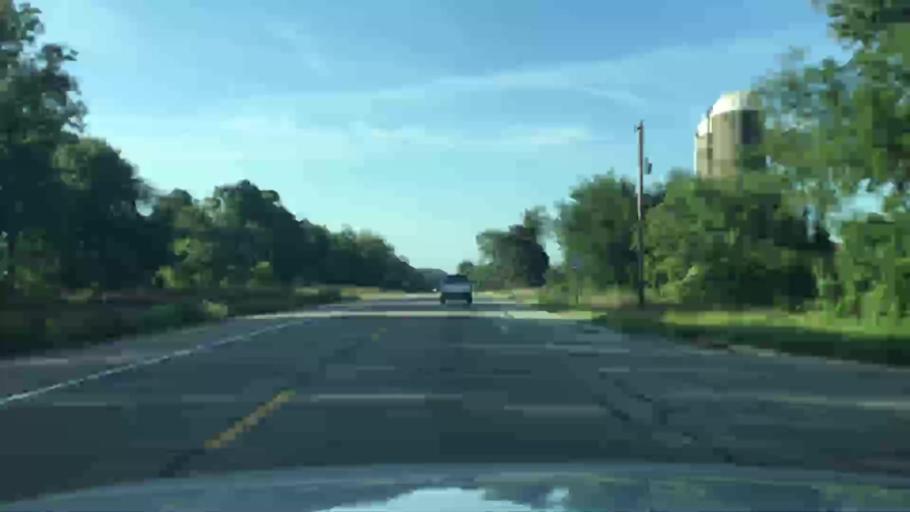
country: US
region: Michigan
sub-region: Jackson County
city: Vandercook Lake
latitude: 42.1030
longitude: -84.3639
